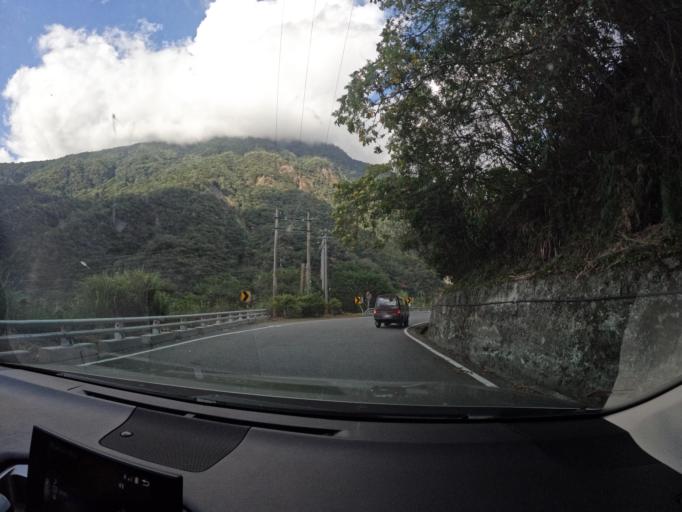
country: TW
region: Taiwan
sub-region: Taitung
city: Taitung
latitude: 23.1539
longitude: 121.0686
